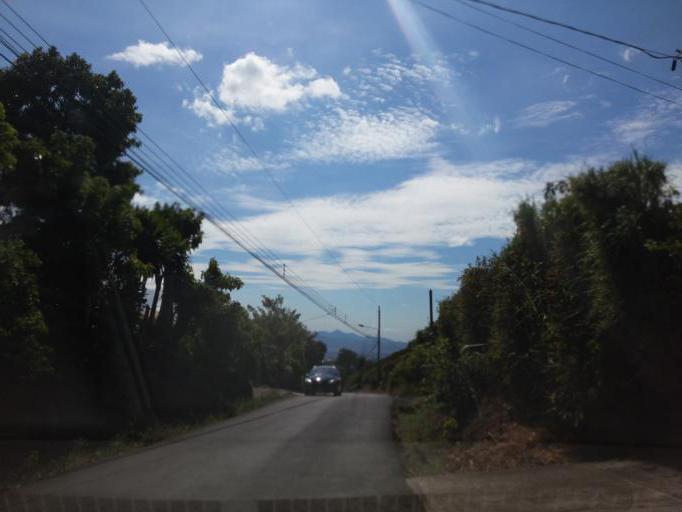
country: CR
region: Heredia
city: Santo Domingo
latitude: 10.0577
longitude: -84.1492
